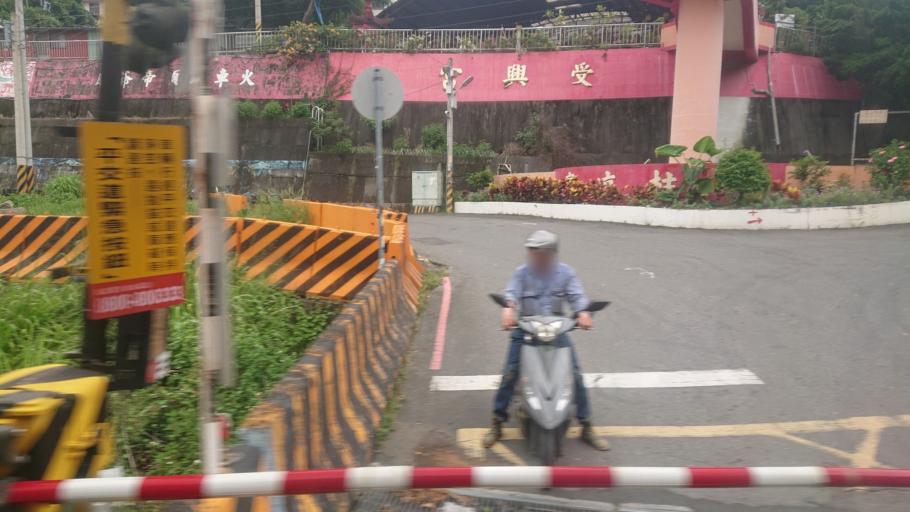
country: TW
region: Taiwan
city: Lugu
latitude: 23.8198
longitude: 120.8549
